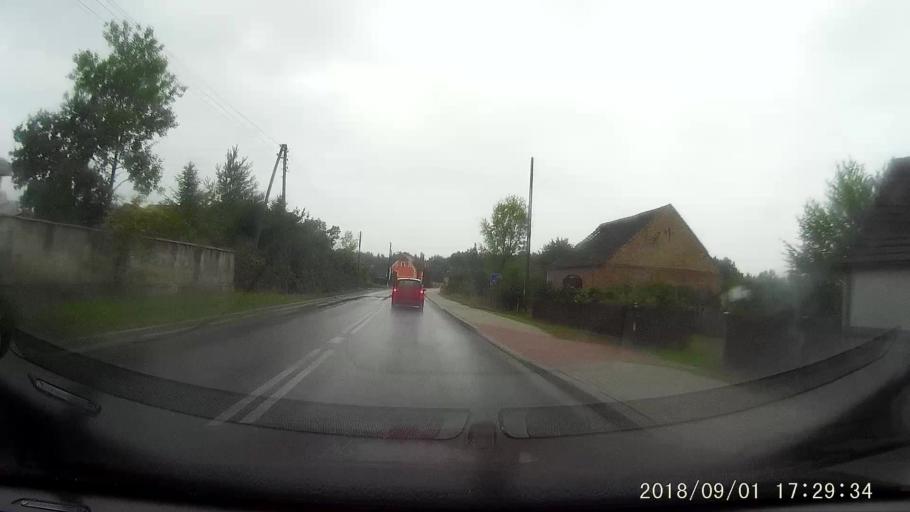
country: PL
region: Lubusz
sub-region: Powiat zaganski
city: Zagan
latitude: 51.6494
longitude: 15.3165
